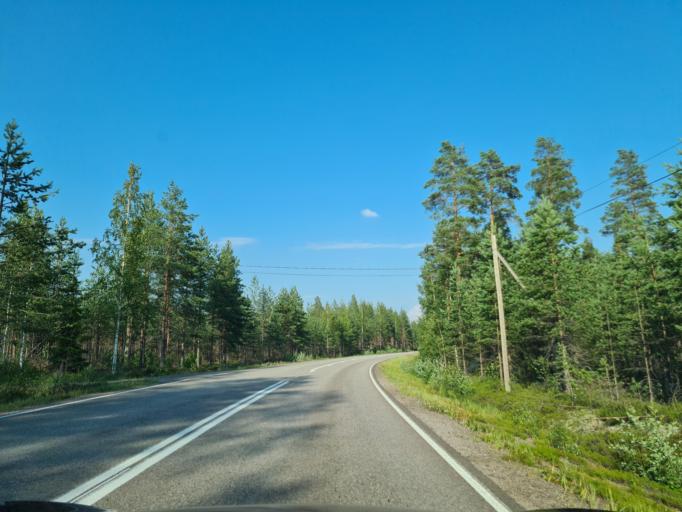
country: FI
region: Satakunta
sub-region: Pohjois-Satakunta
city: Karvia
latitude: 62.3228
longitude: 22.6741
